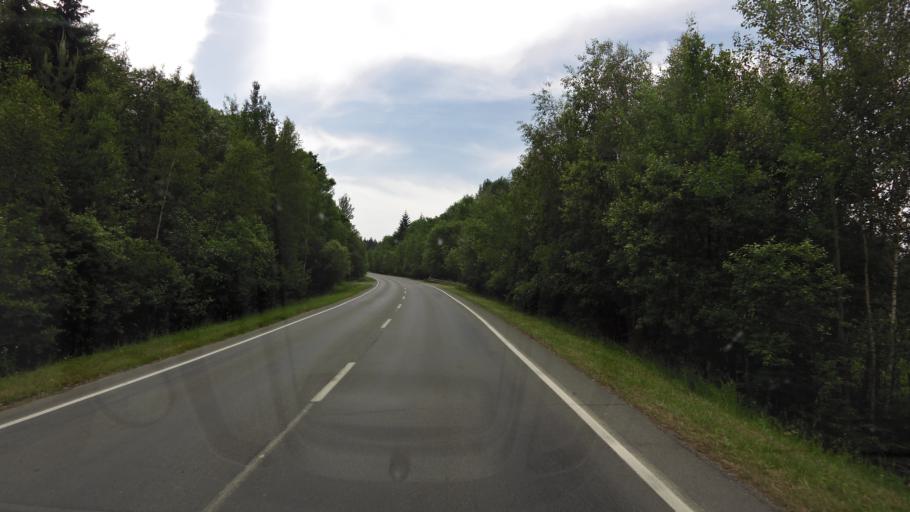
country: CZ
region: Plzensky
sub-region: Okres Rokycany
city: Rokycany
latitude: 49.7123
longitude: 13.5486
